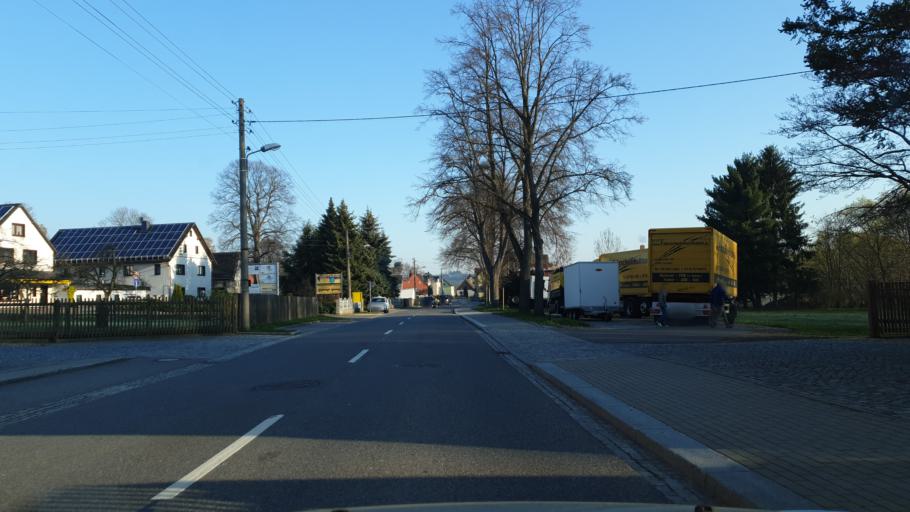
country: DE
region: Saxony
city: Oberlungwitz
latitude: 50.7700
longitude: 12.7046
